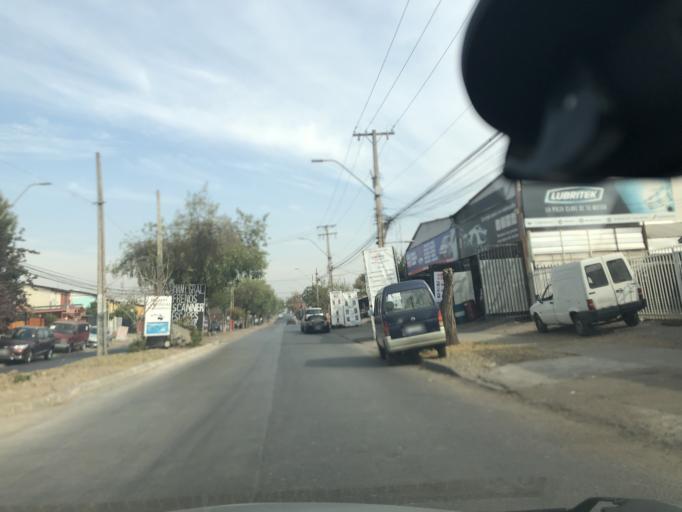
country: CL
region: Santiago Metropolitan
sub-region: Provincia de Cordillera
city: Puente Alto
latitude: -33.5753
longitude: -70.5583
